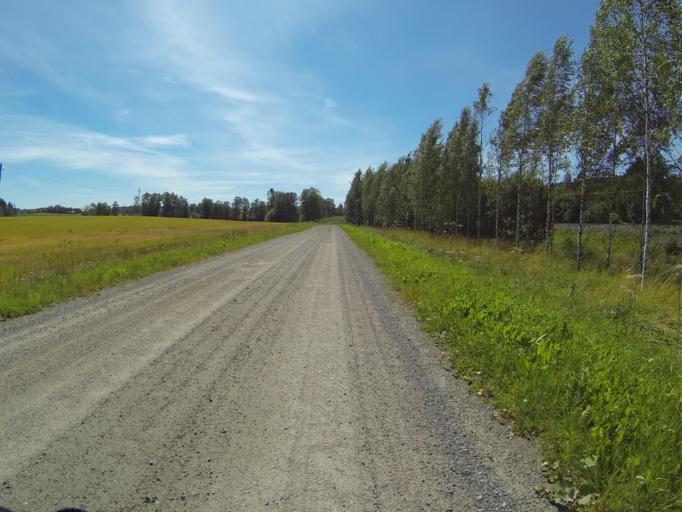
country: FI
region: Varsinais-Suomi
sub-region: Salo
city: Salo
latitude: 60.3109
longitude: 23.1075
